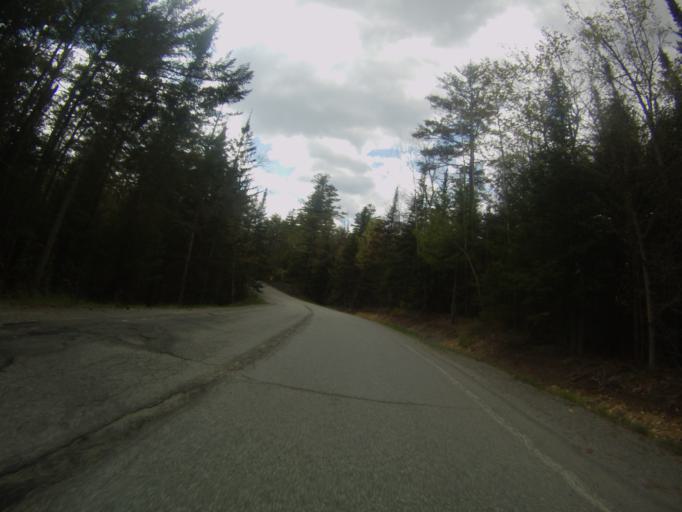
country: US
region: New York
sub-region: Essex County
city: Mineville
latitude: 44.0759
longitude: -73.6450
